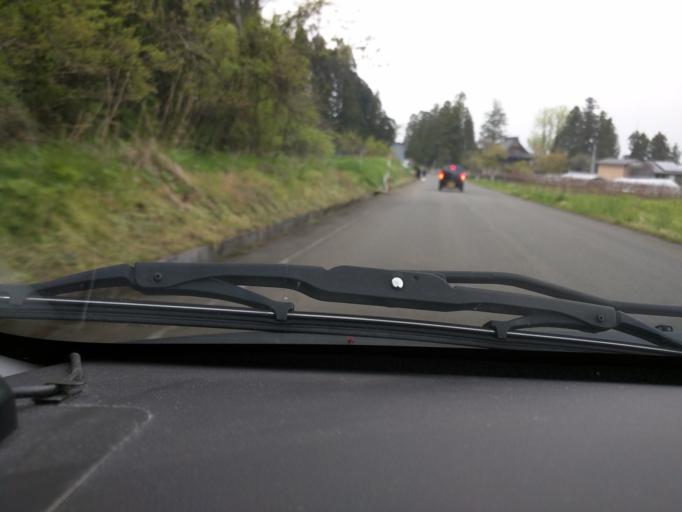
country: JP
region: Fukushima
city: Kitakata
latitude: 37.5008
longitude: 139.8216
